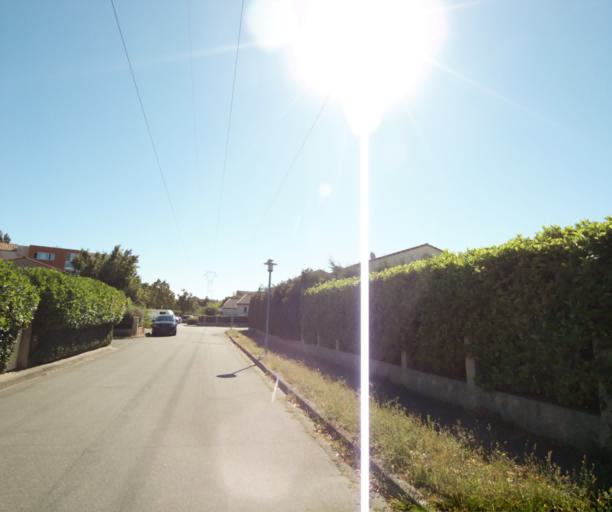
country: FR
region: Midi-Pyrenees
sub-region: Departement de la Haute-Garonne
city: Castanet-Tolosan
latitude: 43.5203
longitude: 1.5030
